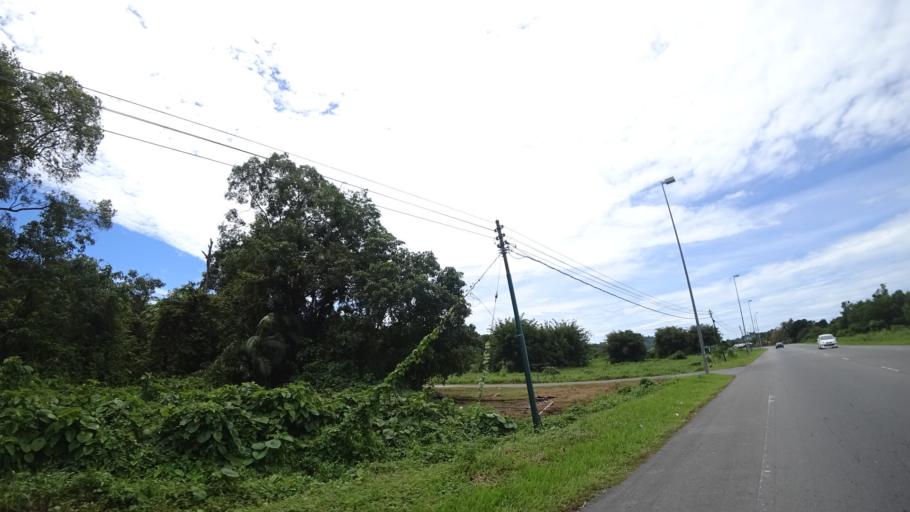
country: BN
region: Tutong
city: Tutong
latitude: 4.7790
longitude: 114.8190
